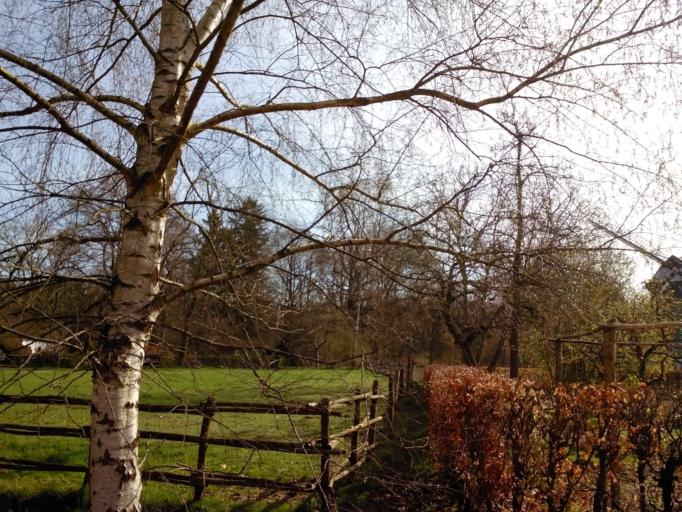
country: BE
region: Flanders
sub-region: Provincie Limburg
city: Zonhoven
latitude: 50.9652
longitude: 5.4062
